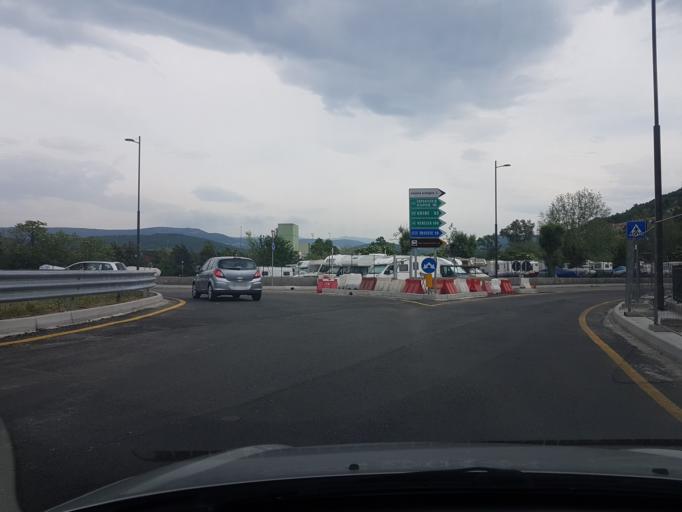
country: IT
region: Friuli Venezia Giulia
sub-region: Provincia di Trieste
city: Muggia
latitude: 45.5975
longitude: 13.7847
